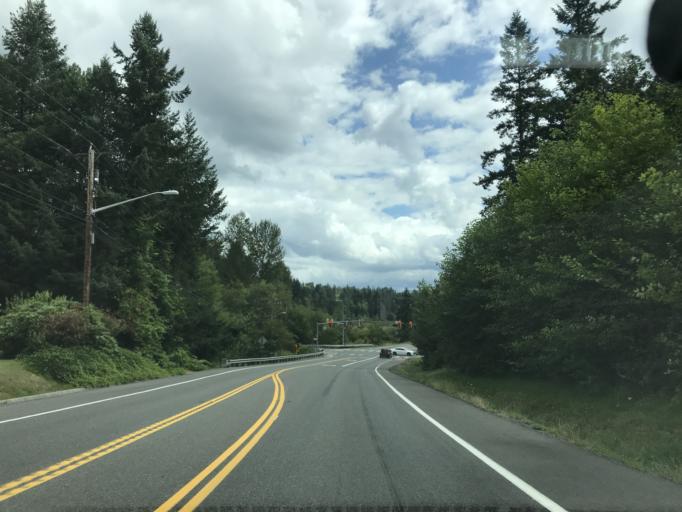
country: US
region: Washington
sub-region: King County
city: Maple Heights-Lake Desire
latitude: 47.4229
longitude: -122.0847
